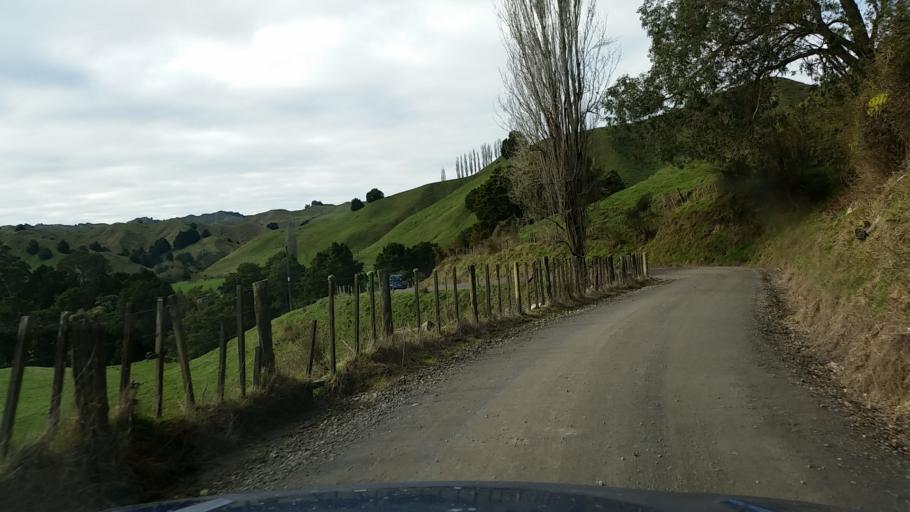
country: NZ
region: Taranaki
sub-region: New Plymouth District
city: Waitara
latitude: -39.0746
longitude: 174.8084
